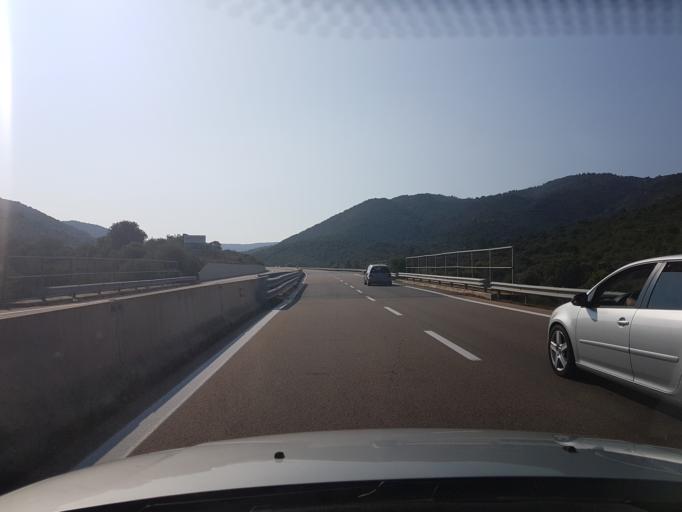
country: IT
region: Sardinia
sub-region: Provincia di Olbia-Tempio
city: Loiri Porto San Paolo
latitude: 40.8351
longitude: 9.5576
